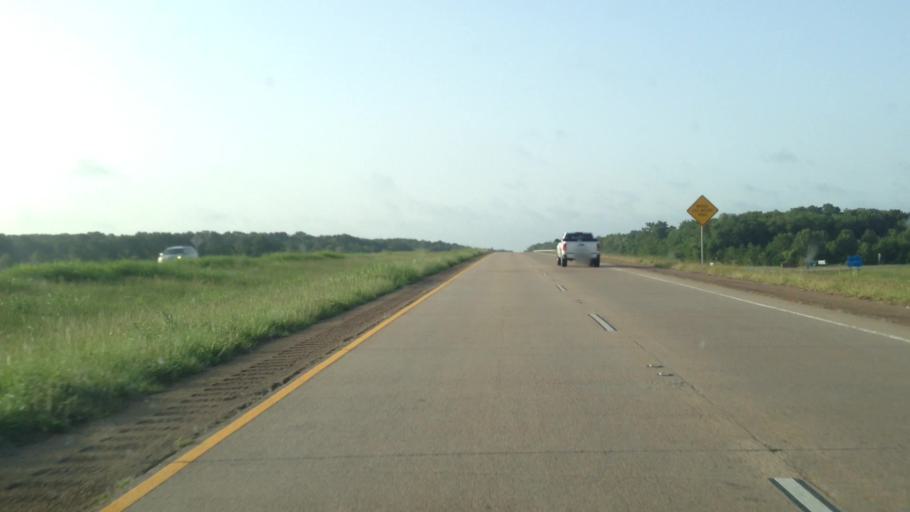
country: US
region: Louisiana
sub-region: Rapides Parish
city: Woodworth
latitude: 31.1671
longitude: -92.4613
